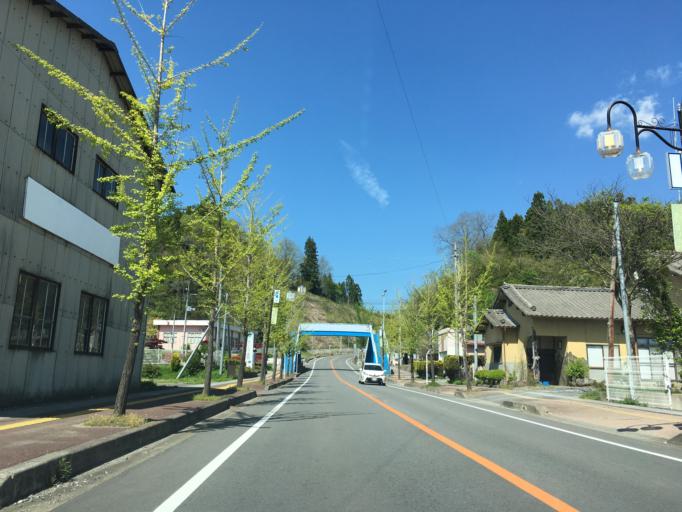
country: JP
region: Fukushima
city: Funehikimachi-funehiki
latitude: 37.2798
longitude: 140.6313
